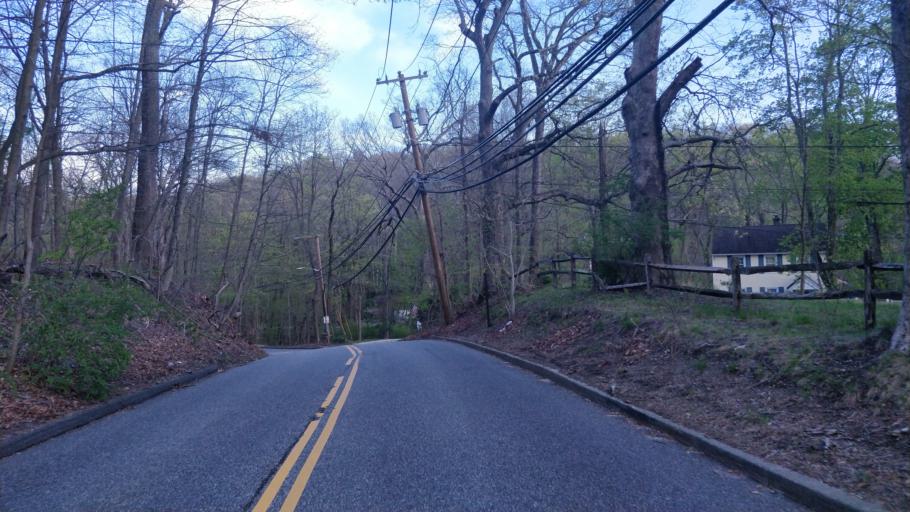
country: US
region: New York
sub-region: Suffolk County
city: Village of the Branch
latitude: 40.8704
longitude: -73.1911
